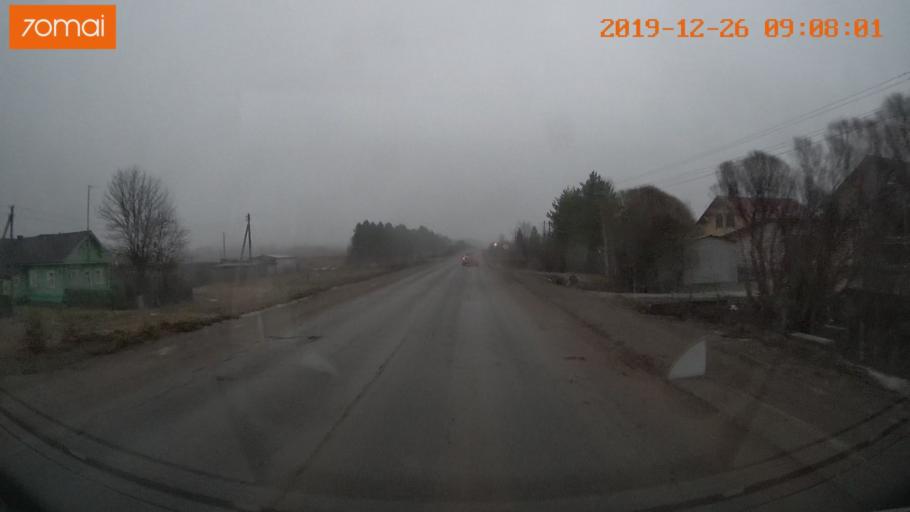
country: RU
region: Vologda
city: Gryazovets
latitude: 58.8522
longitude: 40.2472
